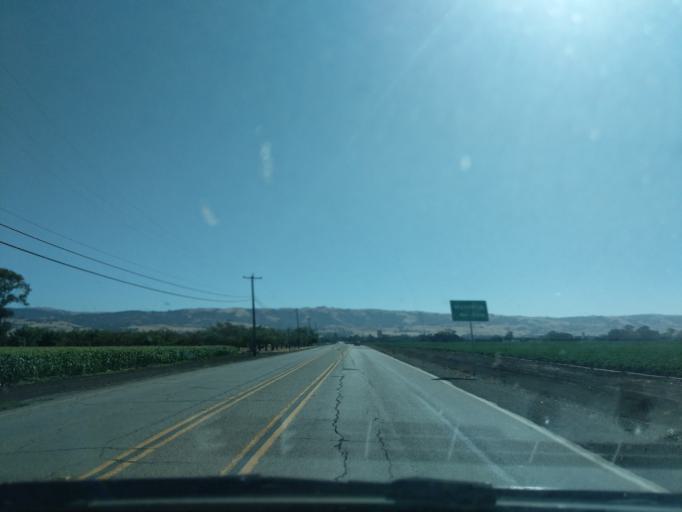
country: US
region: California
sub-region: Santa Clara County
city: Gilroy
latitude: 37.0265
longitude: -121.5558
